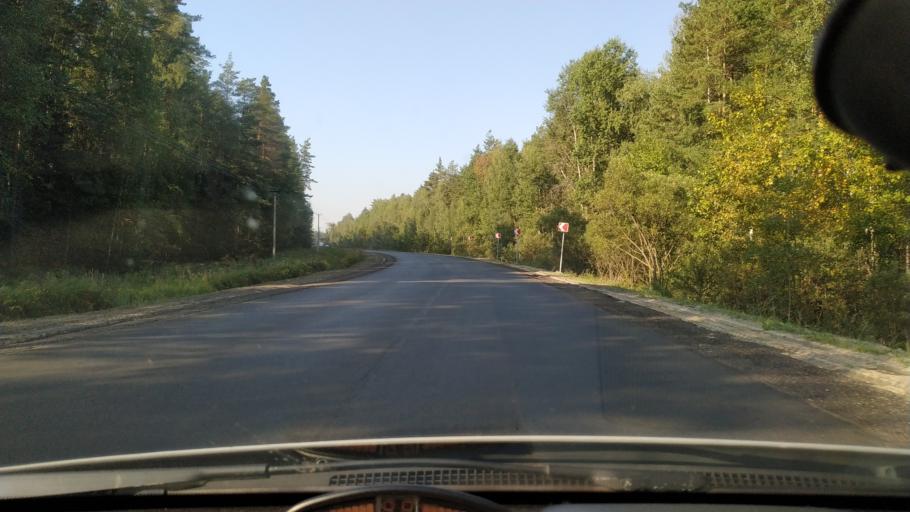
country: RU
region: Moskovskaya
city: Misheronskiy
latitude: 55.6253
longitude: 39.7350
